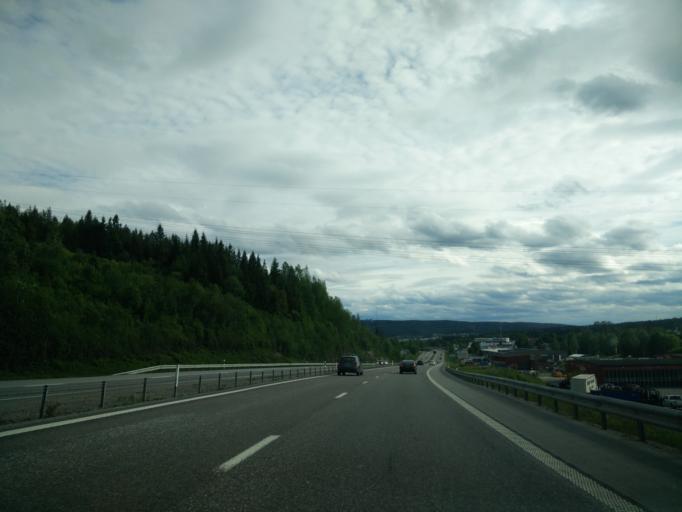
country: SE
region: Vaesternorrland
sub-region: Sundsvalls Kommun
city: Johannedal
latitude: 62.4223
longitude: 17.3487
